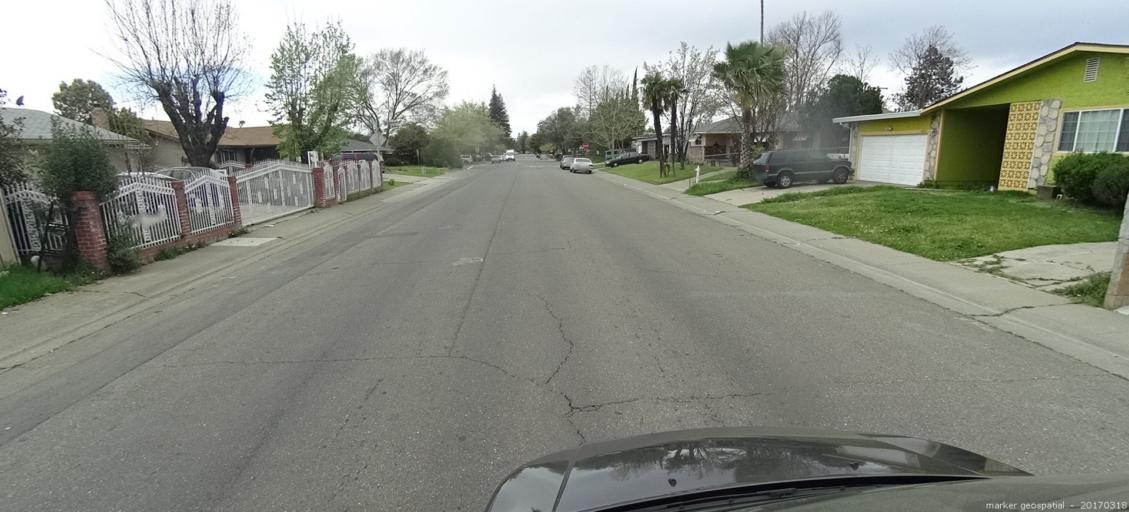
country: US
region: California
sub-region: Sacramento County
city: Parkway
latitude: 38.4816
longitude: -121.4343
